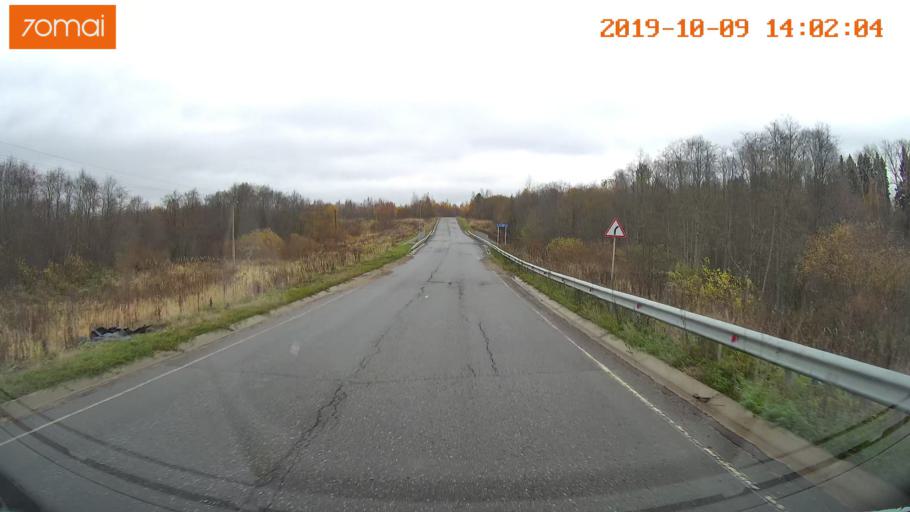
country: RU
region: Kostroma
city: Buy
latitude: 58.4472
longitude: 41.3524
